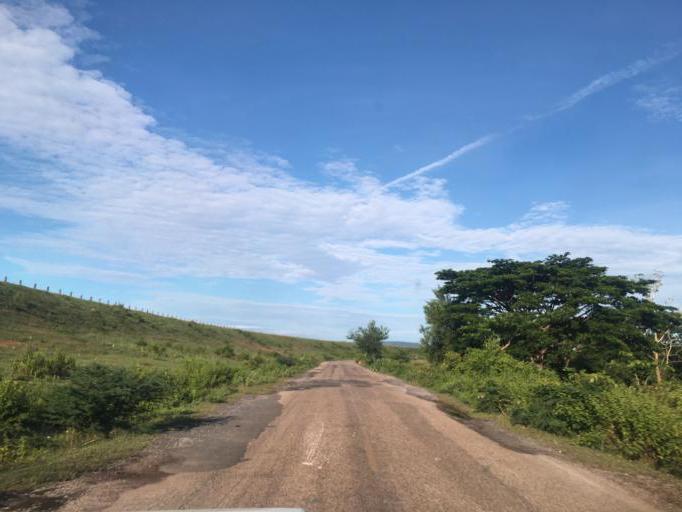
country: TH
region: Changwat Udon Thani
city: Kut Chap
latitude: 17.3617
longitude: 102.5799
